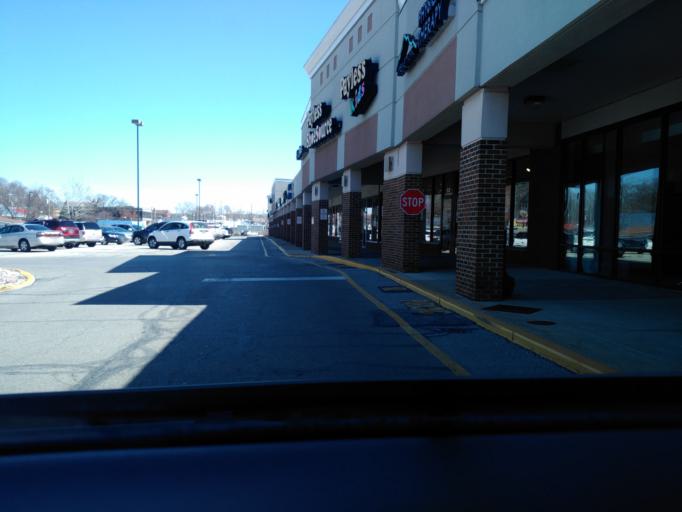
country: US
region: Missouri
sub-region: Saint Louis County
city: Fenton
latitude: 38.5116
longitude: -90.4425
